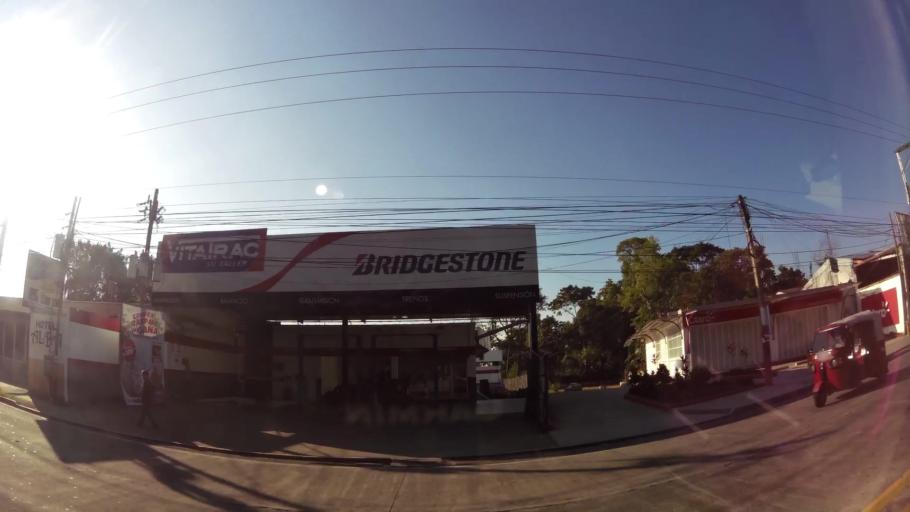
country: GT
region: Suchitepeque
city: Mazatenango
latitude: 14.5331
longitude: -91.5129
